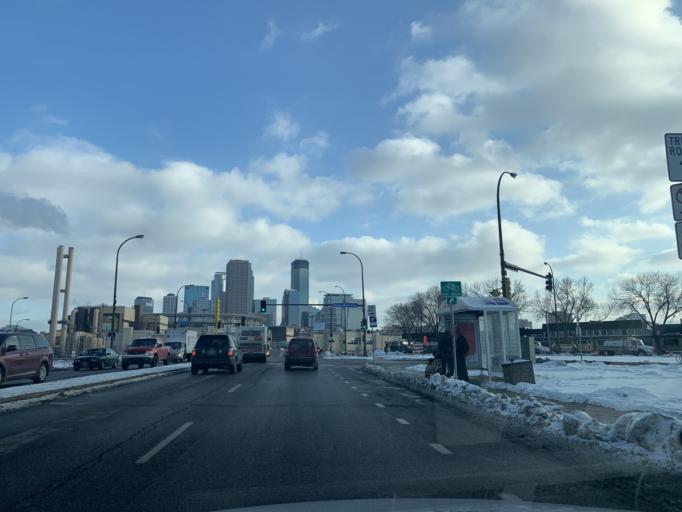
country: US
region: Minnesota
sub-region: Hennepin County
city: Minneapolis
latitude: 44.9848
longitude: -93.2844
